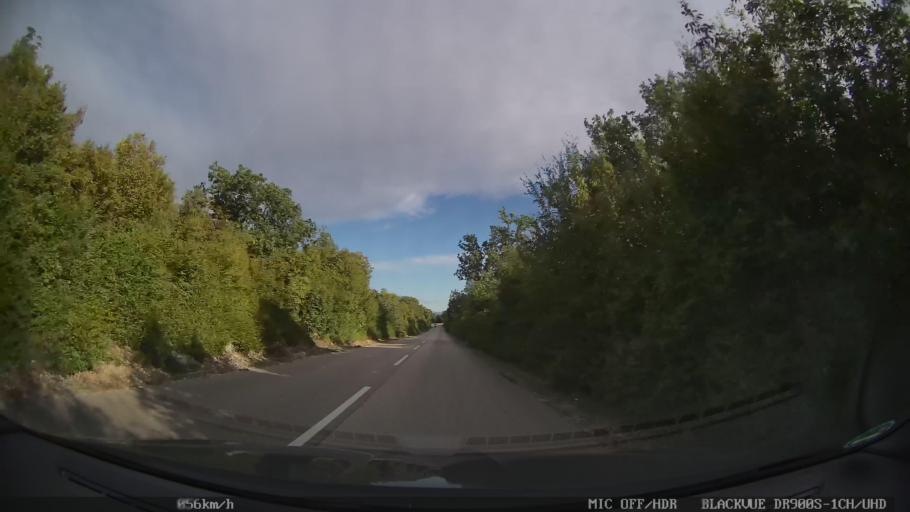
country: HR
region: Primorsko-Goranska
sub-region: Grad Krk
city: Krk
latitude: 45.0657
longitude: 14.4731
